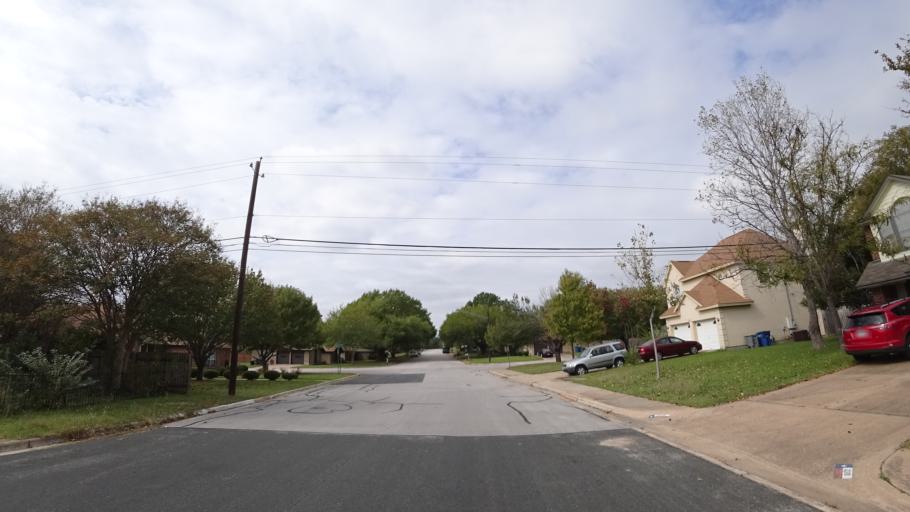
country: US
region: Texas
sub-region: Travis County
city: Wells Branch
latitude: 30.4254
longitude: -97.6962
